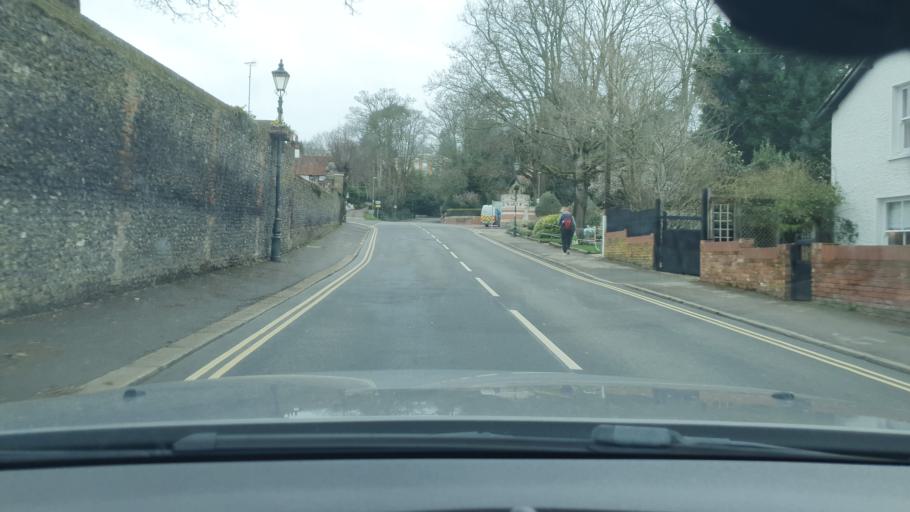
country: GB
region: England
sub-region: Oxfordshire
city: Henley on Thames
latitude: 51.5372
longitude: -0.9096
